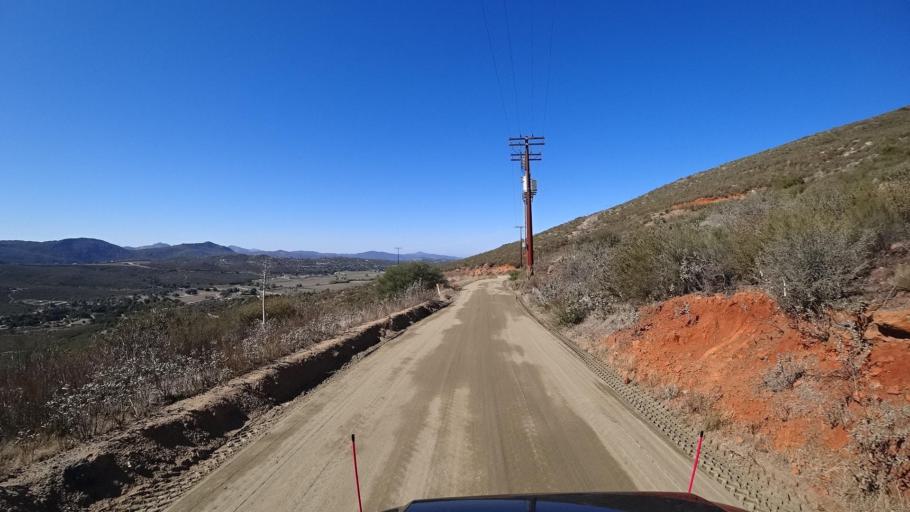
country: US
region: California
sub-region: San Diego County
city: Descanso
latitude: 32.8610
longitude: -116.6751
